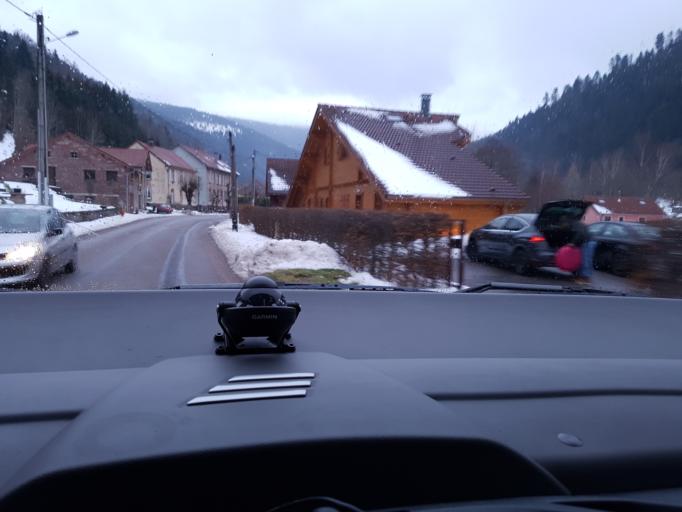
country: FR
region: Lorraine
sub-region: Departement des Vosges
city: Plainfaing
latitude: 48.1460
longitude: 7.0125
